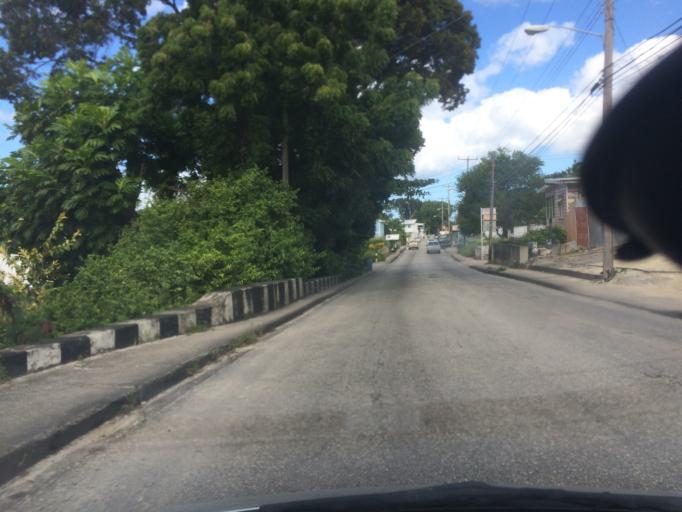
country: BB
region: Saint James
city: Holetown
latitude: 13.1436
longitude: -59.6378
